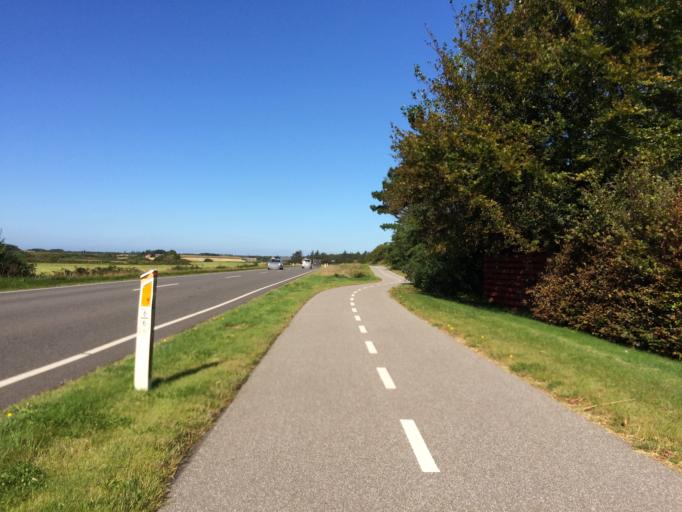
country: DK
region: Central Jutland
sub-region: Holstebro Kommune
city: Ulfborg
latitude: 56.2703
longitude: 8.2211
